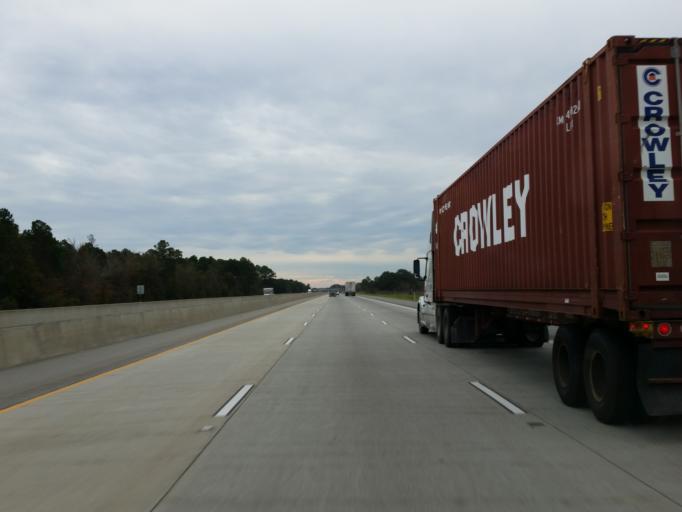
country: US
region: Georgia
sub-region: Tift County
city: Omega
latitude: 31.3087
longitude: -83.4783
